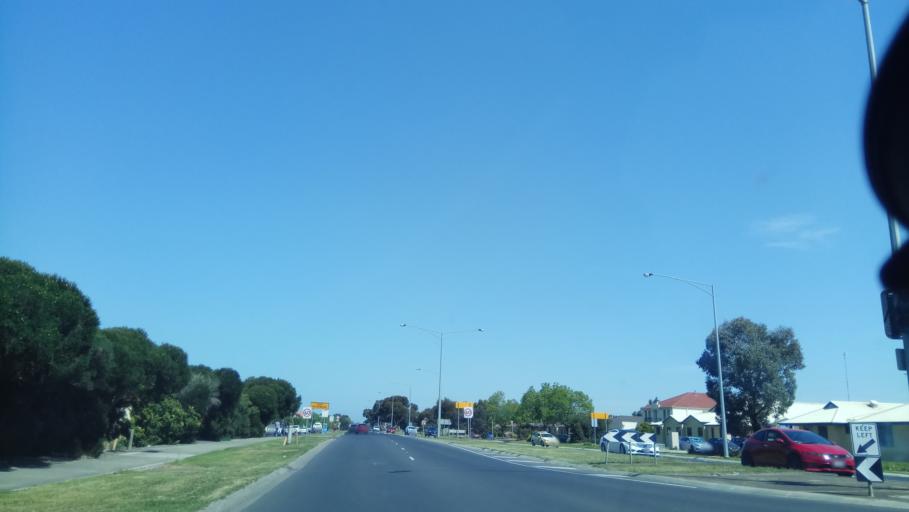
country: AU
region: Victoria
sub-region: Hobsons Bay
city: Altona Meadows
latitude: -37.8872
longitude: 144.7560
